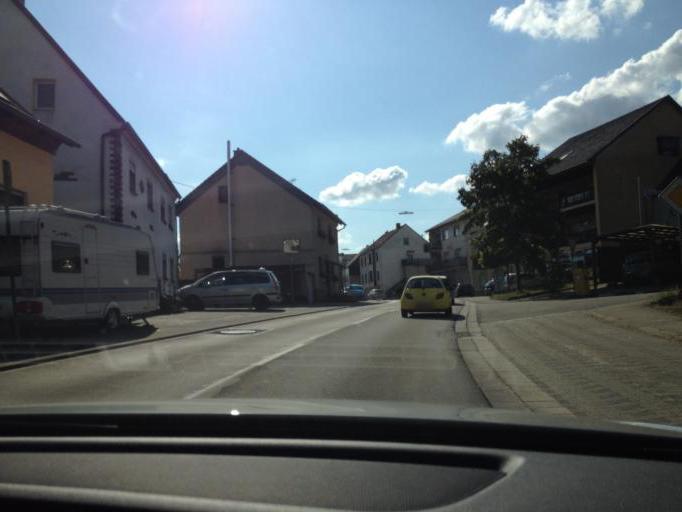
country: DE
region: Saarland
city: Illingen
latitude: 49.3889
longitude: 7.0705
